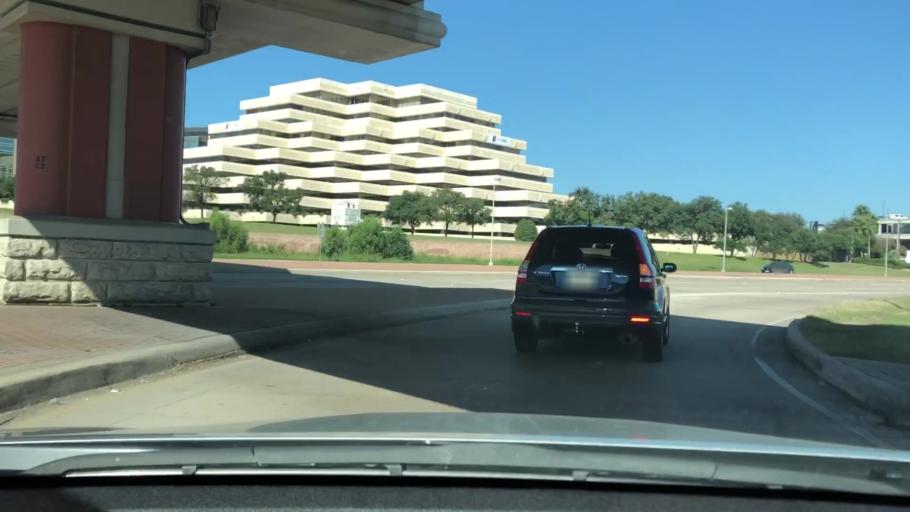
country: US
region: Texas
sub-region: Bexar County
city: Castle Hills
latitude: 29.5210
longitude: -98.4989
